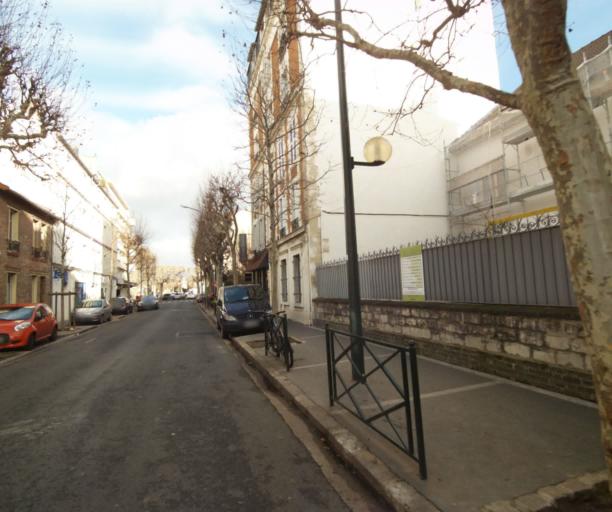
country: FR
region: Ile-de-France
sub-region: Departement des Hauts-de-Seine
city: La Garenne-Colombes
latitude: 48.9056
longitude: 2.2474
